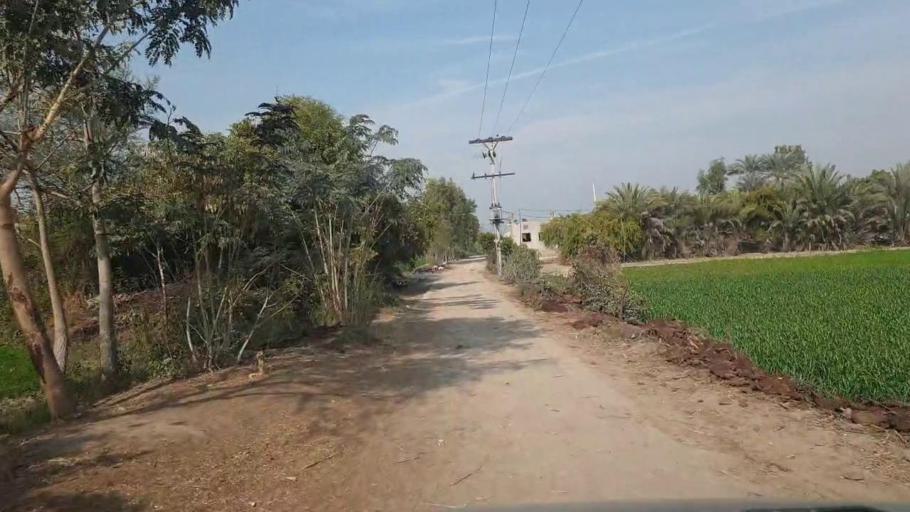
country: PK
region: Sindh
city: Shahdadpur
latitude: 25.8788
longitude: 68.5964
